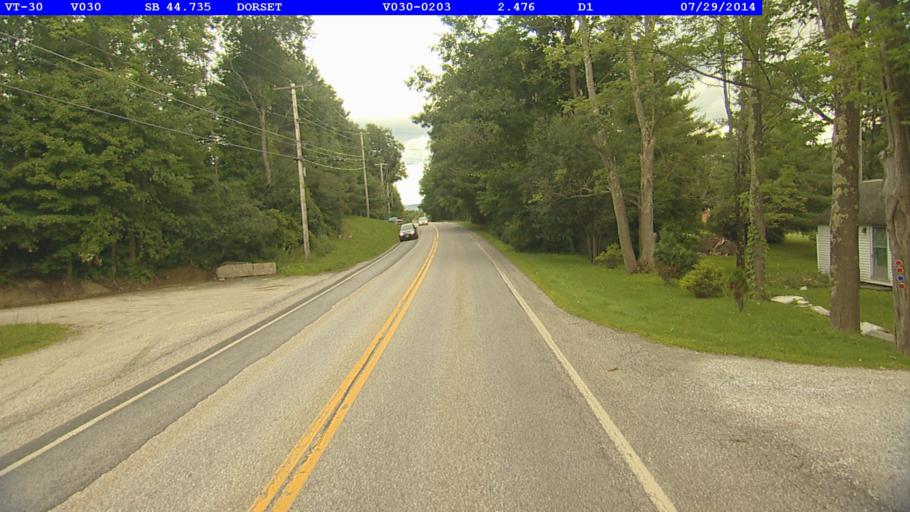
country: US
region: Vermont
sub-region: Bennington County
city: Manchester Center
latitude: 43.2437
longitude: -73.0903
